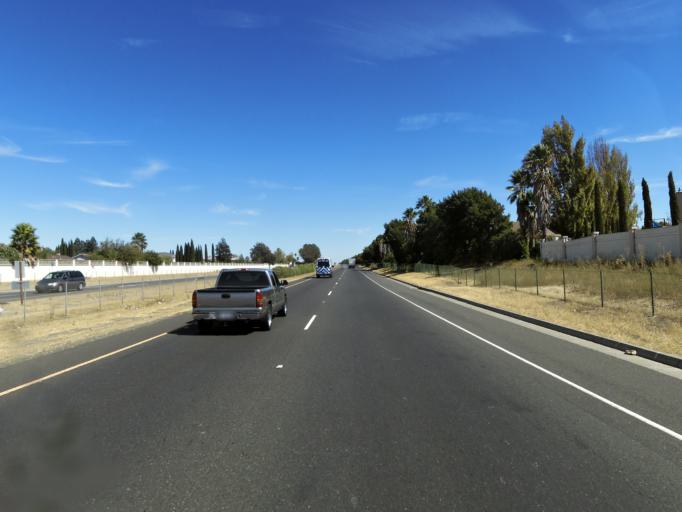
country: US
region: California
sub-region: Solano County
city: Fairfield
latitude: 38.2433
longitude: -122.0151
